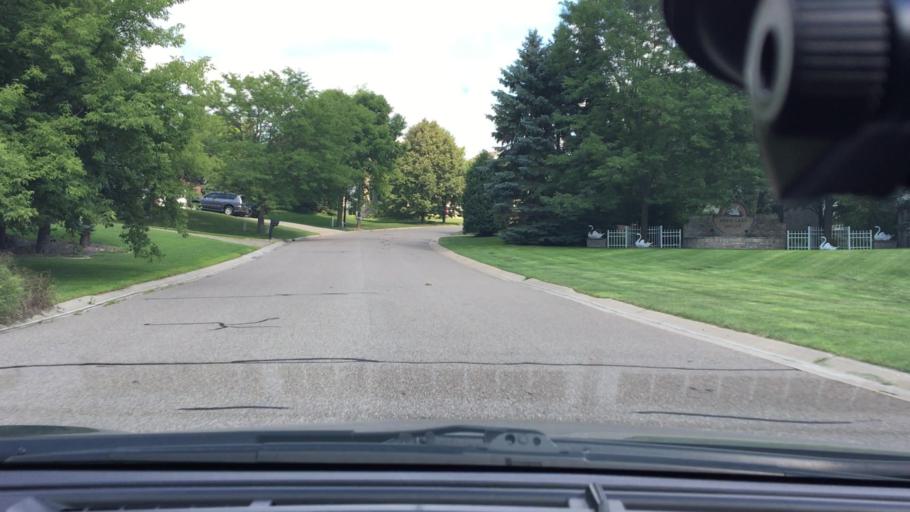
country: US
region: Minnesota
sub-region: Hennepin County
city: Plymouth
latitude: 45.0323
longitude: -93.4449
